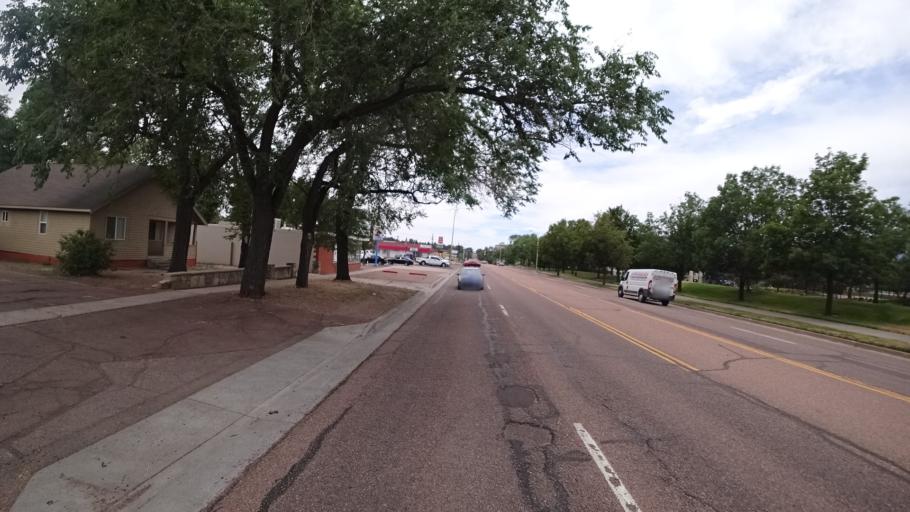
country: US
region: Colorado
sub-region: El Paso County
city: Colorado Springs
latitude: 38.8404
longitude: -104.7942
